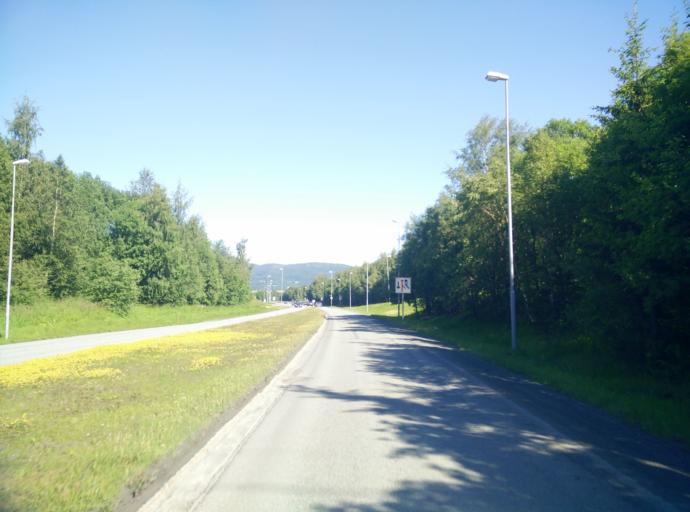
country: NO
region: Sor-Trondelag
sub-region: Trondheim
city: Trondheim
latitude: 63.3703
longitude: 10.3464
